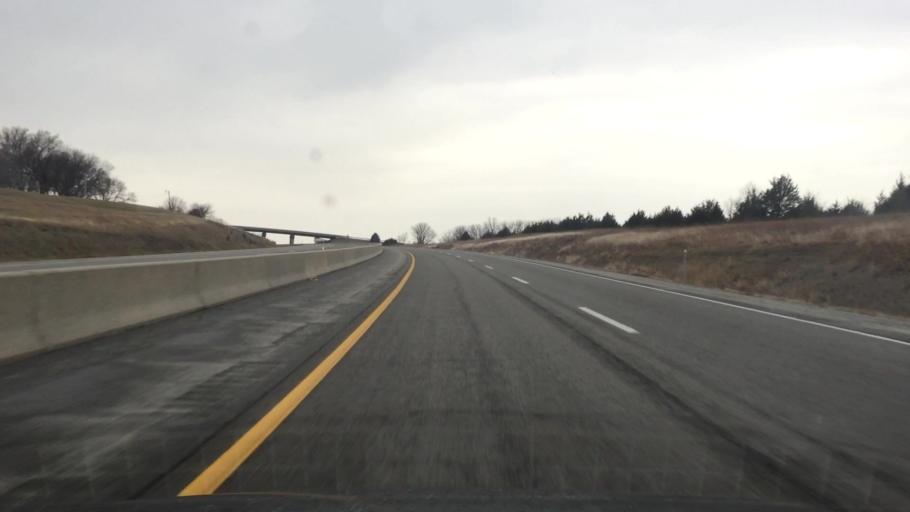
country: US
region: Kansas
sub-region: Shawnee County
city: Auburn
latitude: 38.9593
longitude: -95.7309
